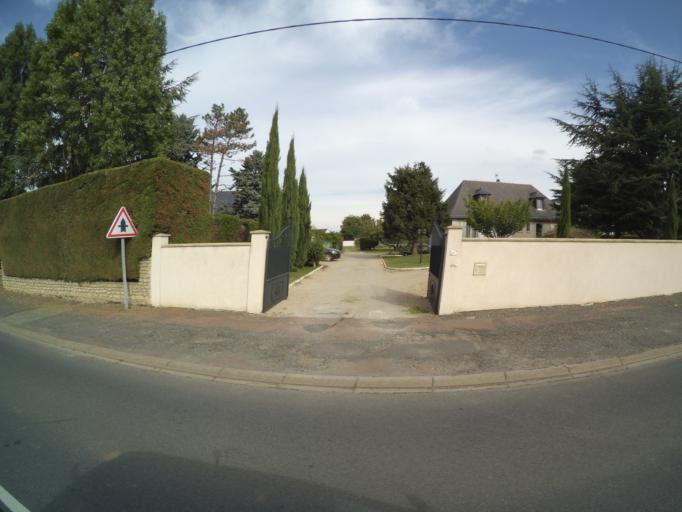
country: FR
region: Pays de la Loire
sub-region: Departement de Maine-et-Loire
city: Doue-la-Fontaine
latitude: 47.1942
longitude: -0.2958
